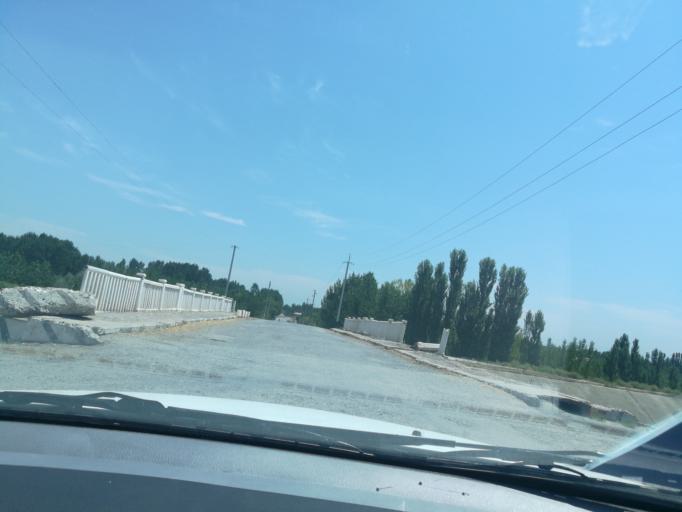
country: UZ
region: Namangan
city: Haqqulobod
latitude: 40.8992
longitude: 72.0032
